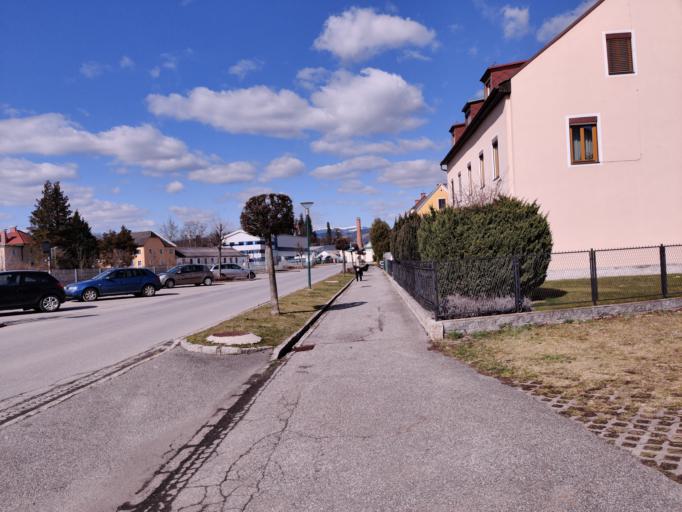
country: AT
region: Styria
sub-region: Politischer Bezirk Voitsberg
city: Voitsberg
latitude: 47.0448
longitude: 15.1490
